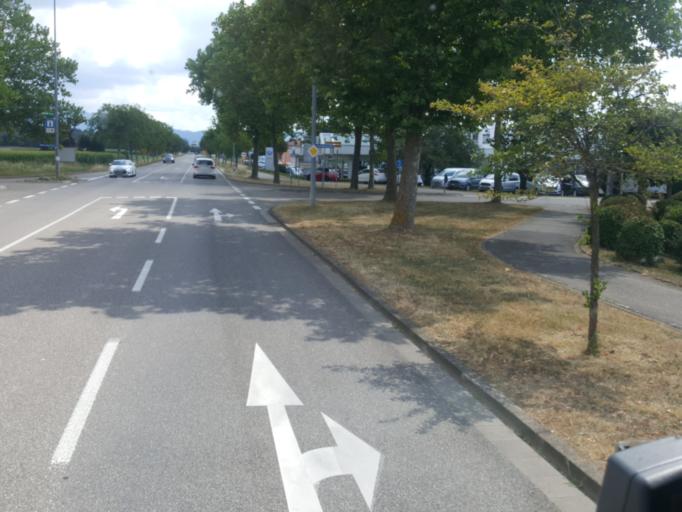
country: DE
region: Baden-Wuerttemberg
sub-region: Freiburg Region
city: Teningen
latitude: 48.1360
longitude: 7.8123
